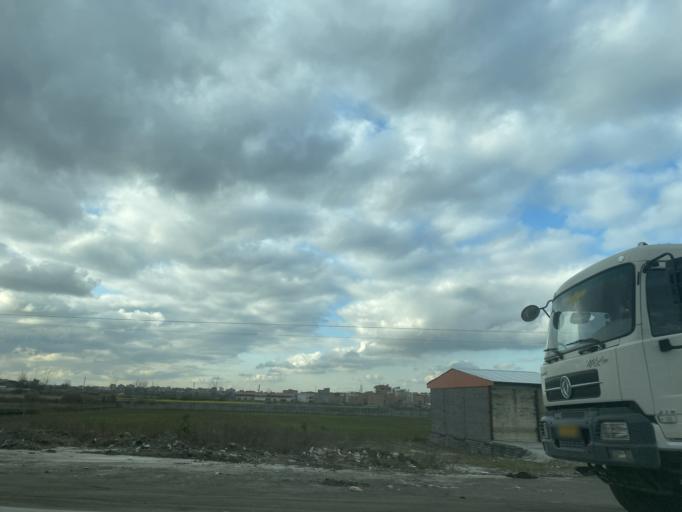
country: IR
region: Mazandaran
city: Amol
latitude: 36.4483
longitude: 52.3918
